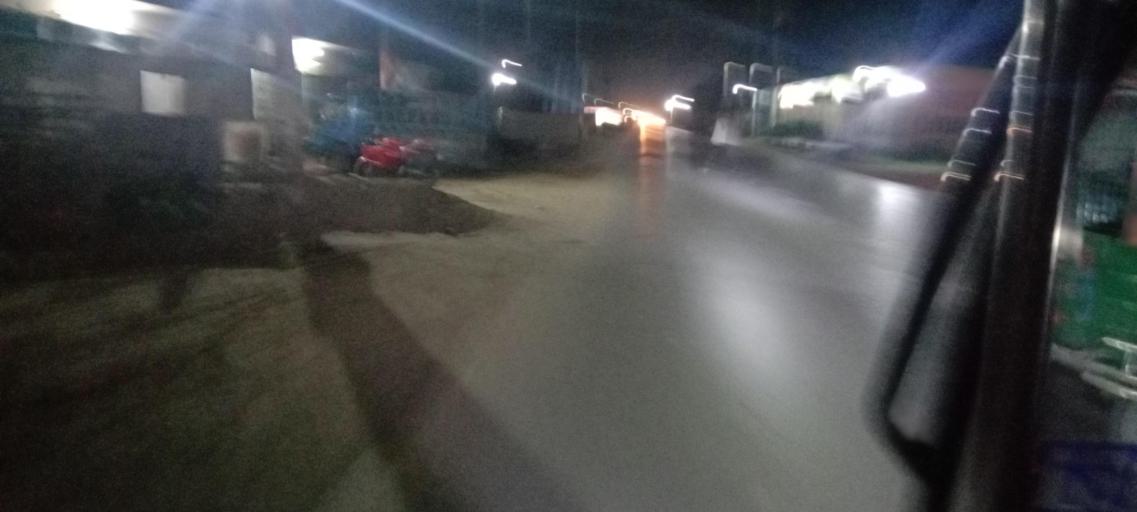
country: BD
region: Dhaka
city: Azimpur
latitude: 23.7000
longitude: 90.3672
